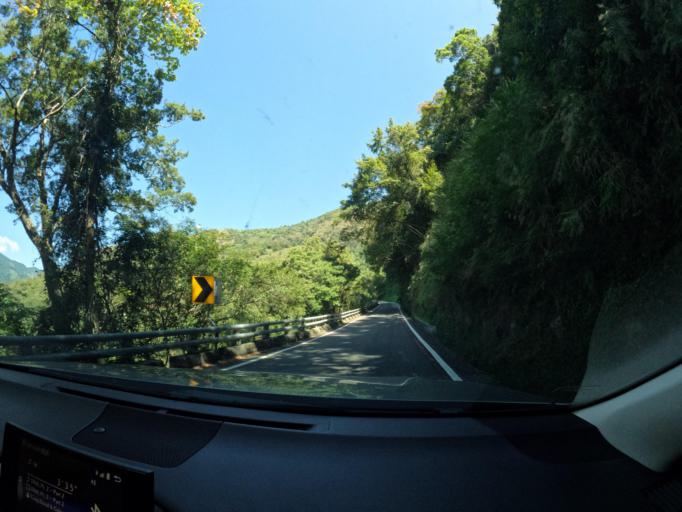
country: TW
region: Taiwan
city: Yujing
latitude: 23.2710
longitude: 120.8446
